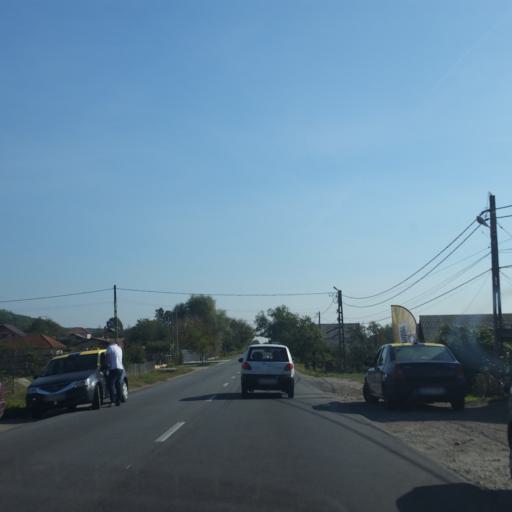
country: RO
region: Arges
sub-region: Municipiul Curtea de Arges
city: Curtea de Arges
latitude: 45.0965
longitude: 24.6715
